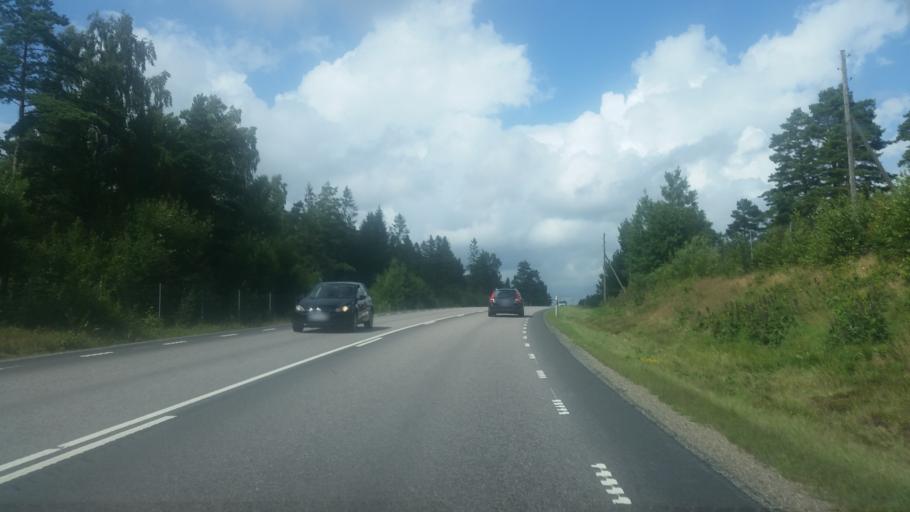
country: SE
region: Vaestra Goetaland
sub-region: Partille Kommun
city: Furulund
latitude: 57.7145
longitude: 12.1430
